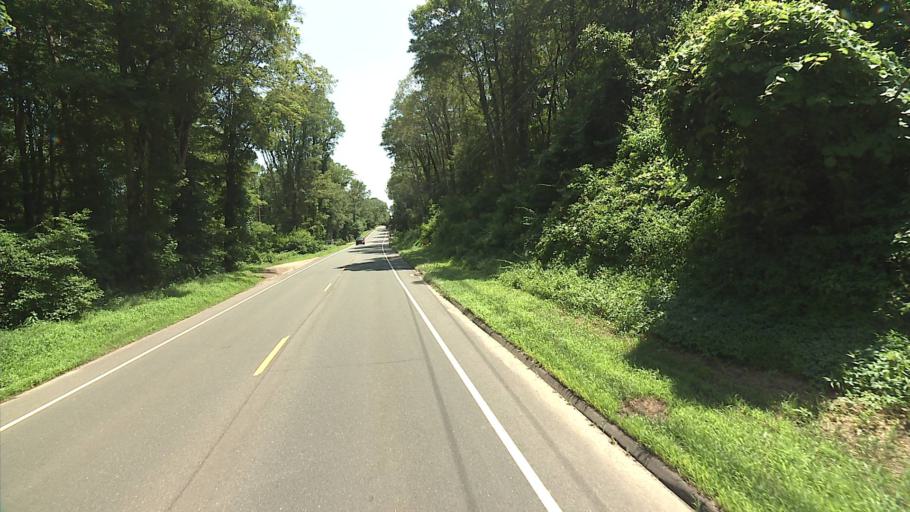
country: US
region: Connecticut
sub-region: Middlesex County
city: East Haddam
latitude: 41.4315
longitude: -72.4541
